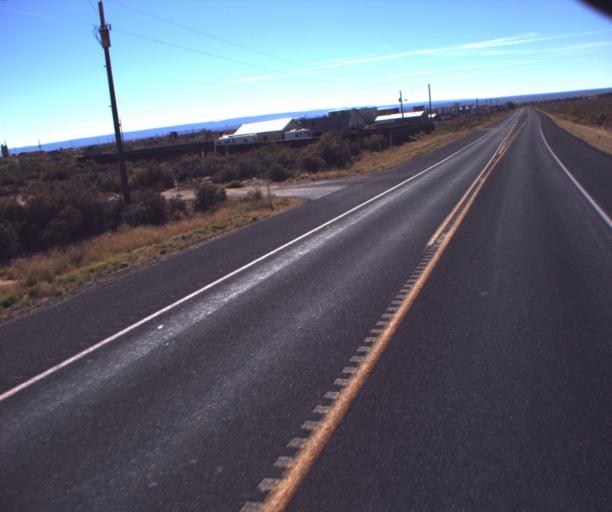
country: US
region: Arizona
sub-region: Coconino County
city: Fredonia
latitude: 36.9772
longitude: -112.5286
